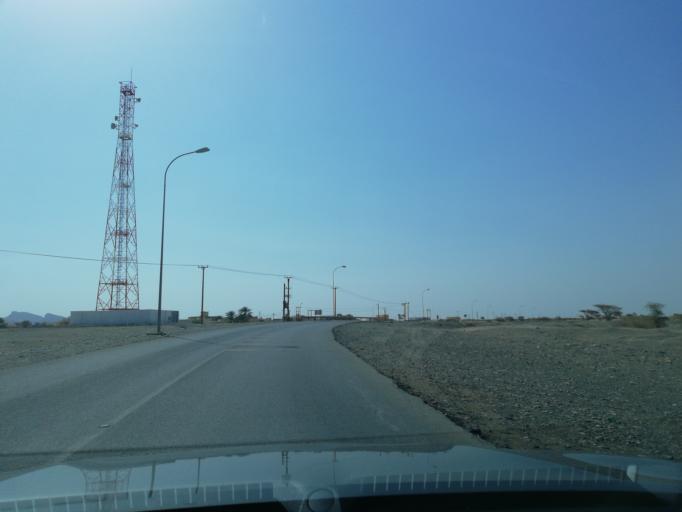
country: OM
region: Muhafazat ad Dakhiliyah
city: Adam
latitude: 22.3665
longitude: 58.0610
